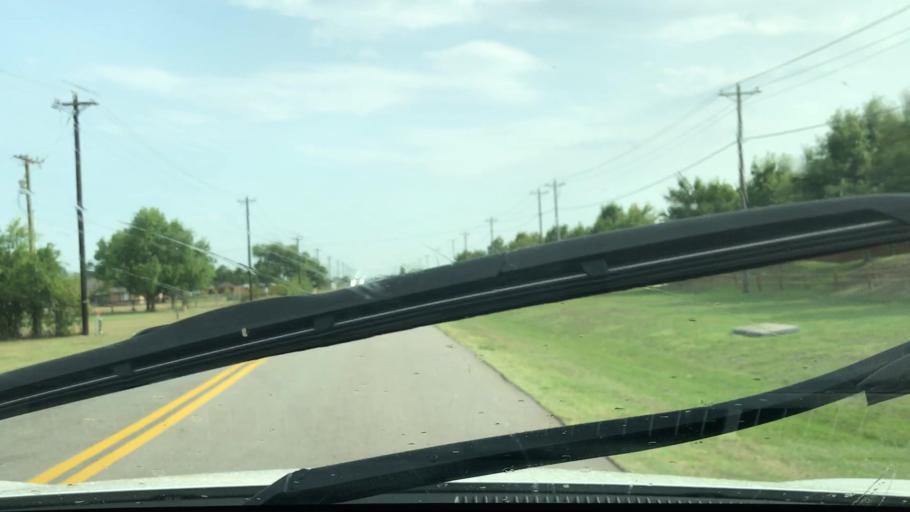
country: US
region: Texas
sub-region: Collin County
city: Wylie
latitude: 32.9882
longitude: -96.5218
